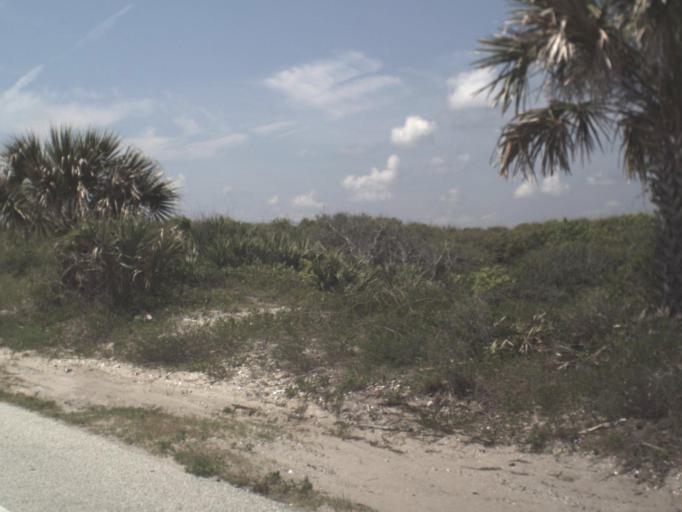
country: US
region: Florida
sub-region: Saint Johns County
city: Palm Valley
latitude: 30.1242
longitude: -81.3477
